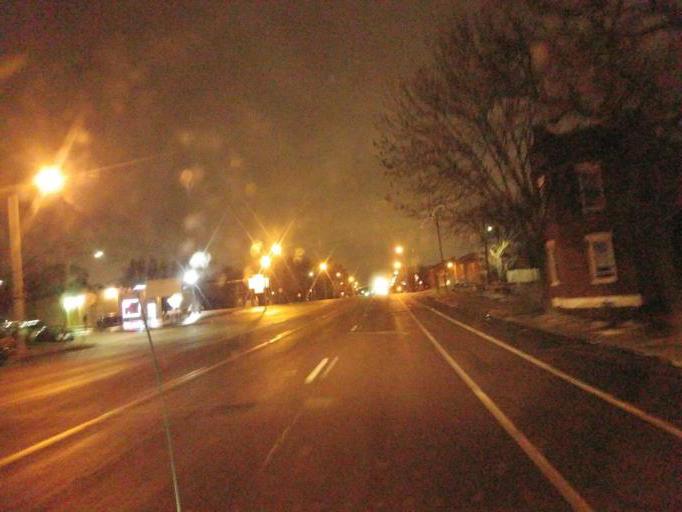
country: US
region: Missouri
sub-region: City of Saint Louis
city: St. Louis
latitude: 38.6526
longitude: -90.2010
